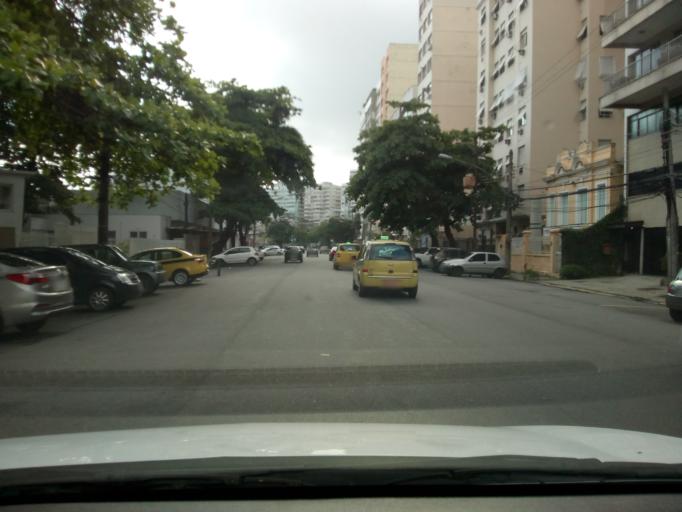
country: BR
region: Rio de Janeiro
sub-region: Rio De Janeiro
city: Rio de Janeiro
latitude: -22.9557
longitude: -43.1800
